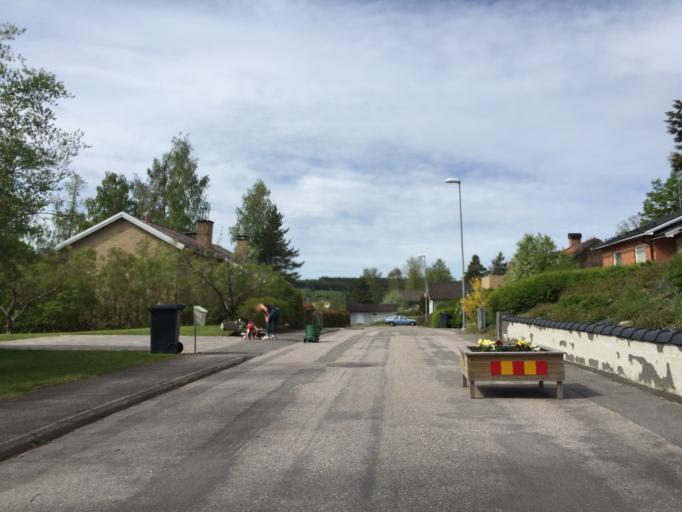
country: SE
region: Dalarna
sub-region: Ludvika Kommun
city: Ludvika
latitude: 60.1347
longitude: 15.1816
